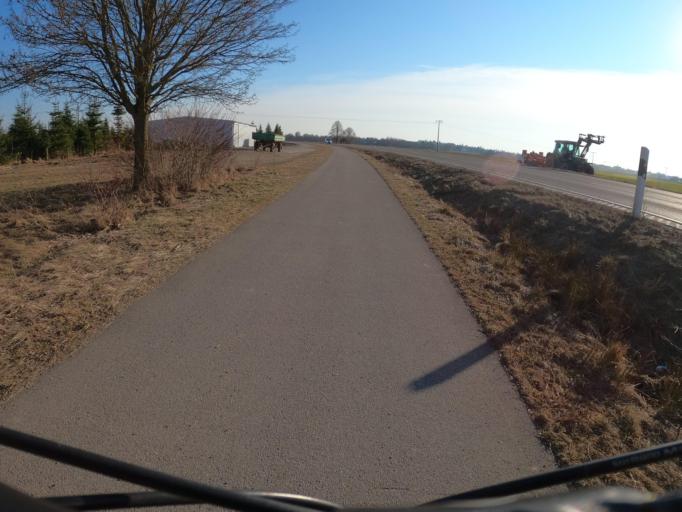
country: DE
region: Bavaria
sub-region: Swabia
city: Neu-Ulm
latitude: 48.4198
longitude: 10.0557
